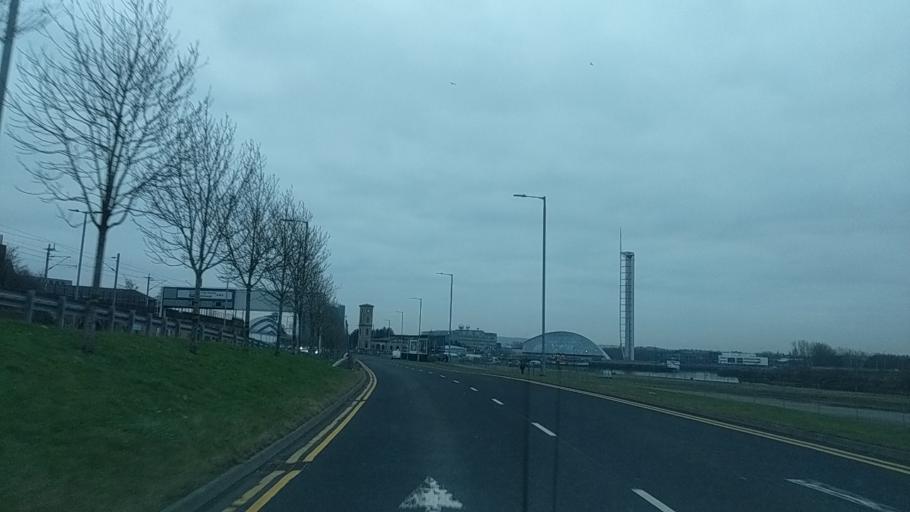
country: GB
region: Scotland
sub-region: Glasgow City
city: Glasgow
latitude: 55.8648
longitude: -4.3014
